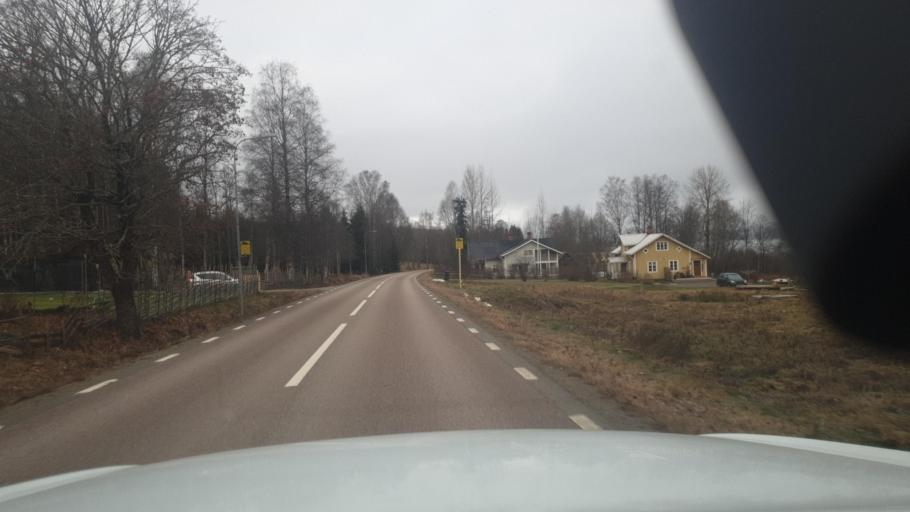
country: SE
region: Vaermland
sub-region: Sunne Kommun
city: Sunne
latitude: 59.8881
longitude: 12.9219
